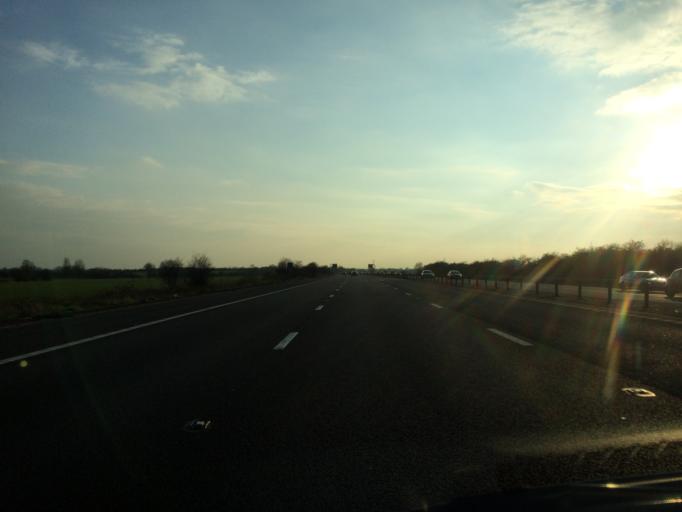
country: GB
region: England
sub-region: Wiltshire
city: Bremhill
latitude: 51.5253
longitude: -2.0371
